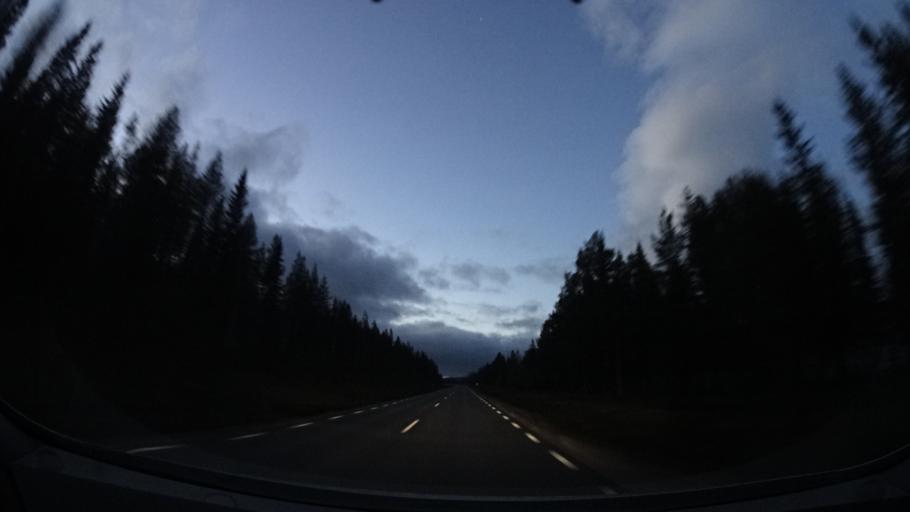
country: SE
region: Vaesterbotten
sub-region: Dorotea Kommun
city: Dorotea
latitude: 64.2345
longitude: 16.8006
